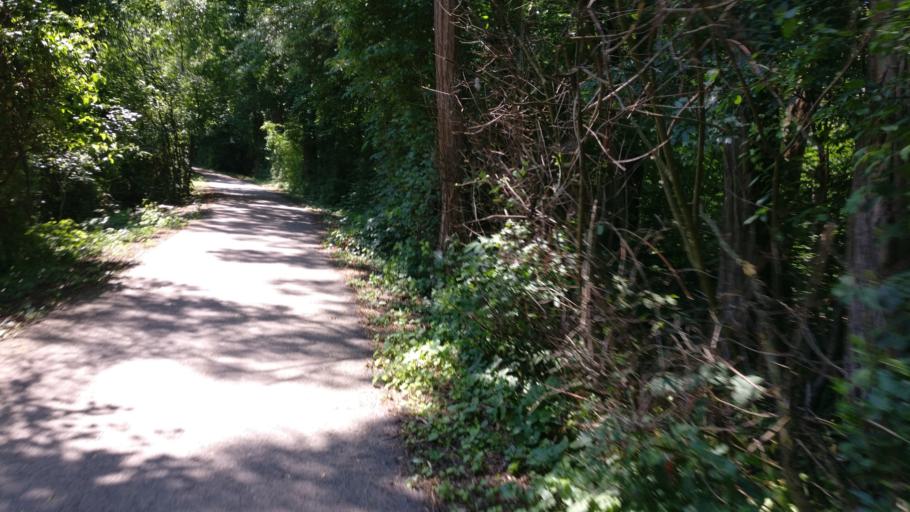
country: AT
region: Lower Austria
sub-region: Politischer Bezirk Baden
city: Oberwaltersdorf
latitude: 47.9658
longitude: 16.3105
